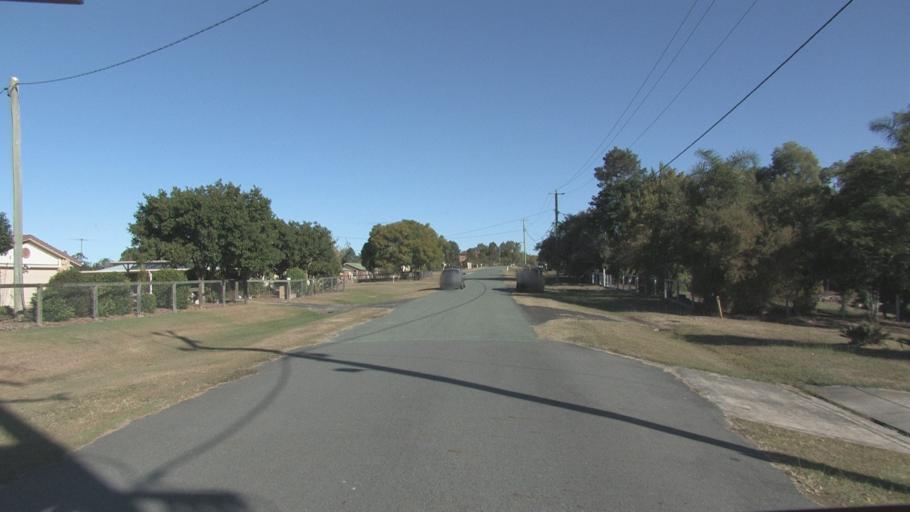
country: AU
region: Queensland
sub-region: Logan
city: North Maclean
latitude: -27.7873
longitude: 153.0252
